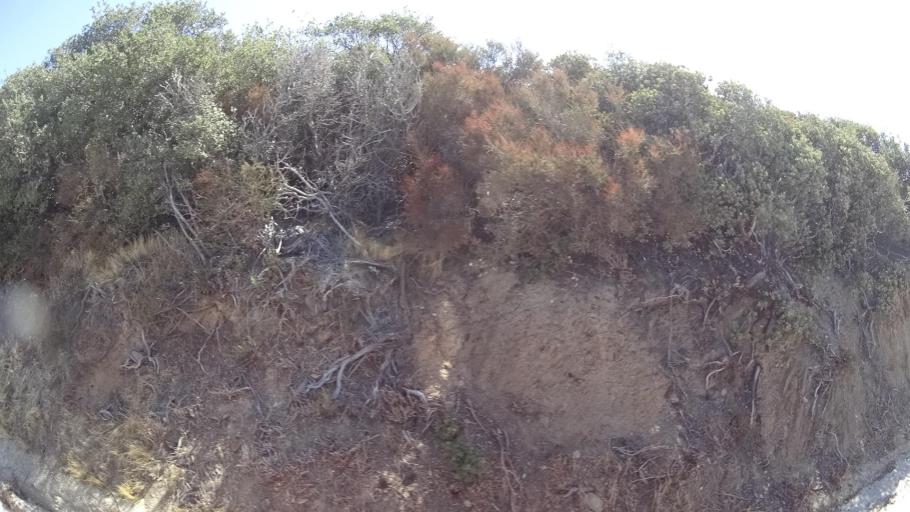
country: US
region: California
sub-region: San Diego County
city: Julian
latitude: 33.0665
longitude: -116.5751
